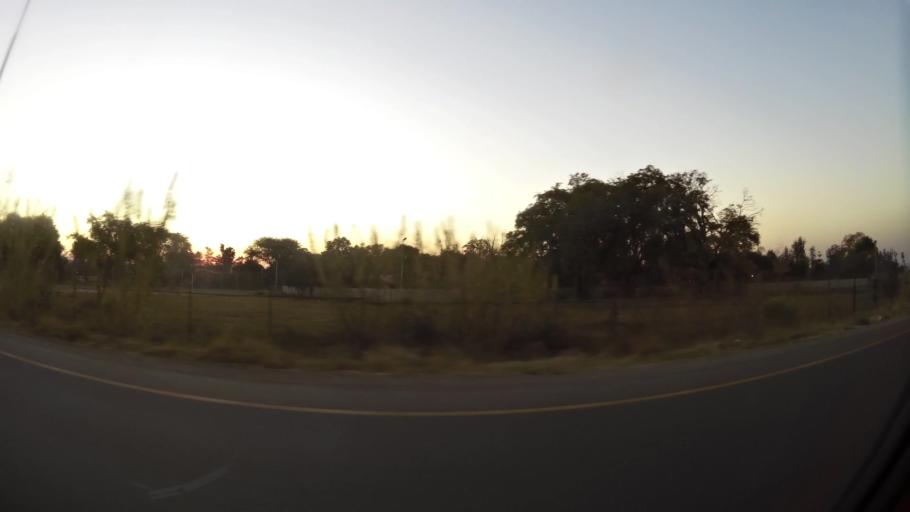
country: ZA
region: North-West
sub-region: Bojanala Platinum District Municipality
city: Rustenburg
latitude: -25.6445
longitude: 27.2593
